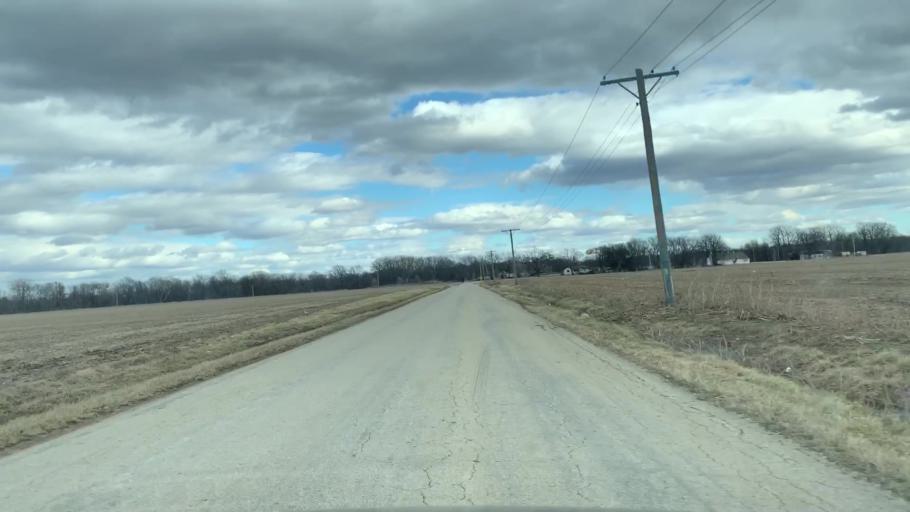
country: US
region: Kansas
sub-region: Allen County
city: Humboldt
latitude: 37.8129
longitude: -95.4577
